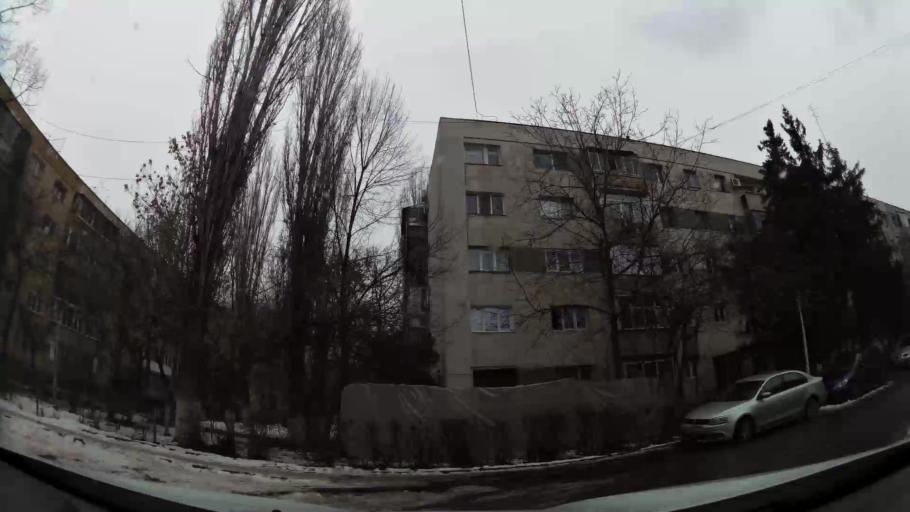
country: RO
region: Ilfov
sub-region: Comuna Chiajna
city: Rosu
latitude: 44.4243
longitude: 26.0260
